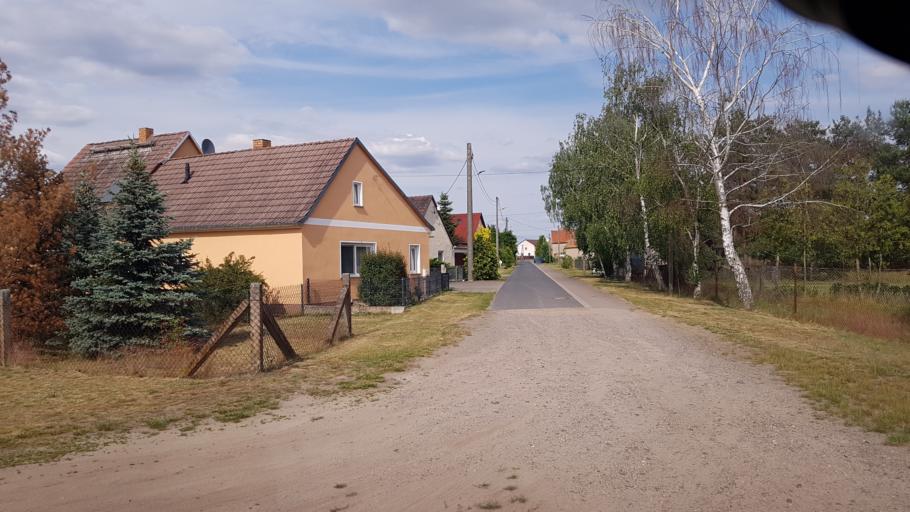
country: DE
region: Brandenburg
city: Herzberg
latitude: 51.7596
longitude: 13.2493
